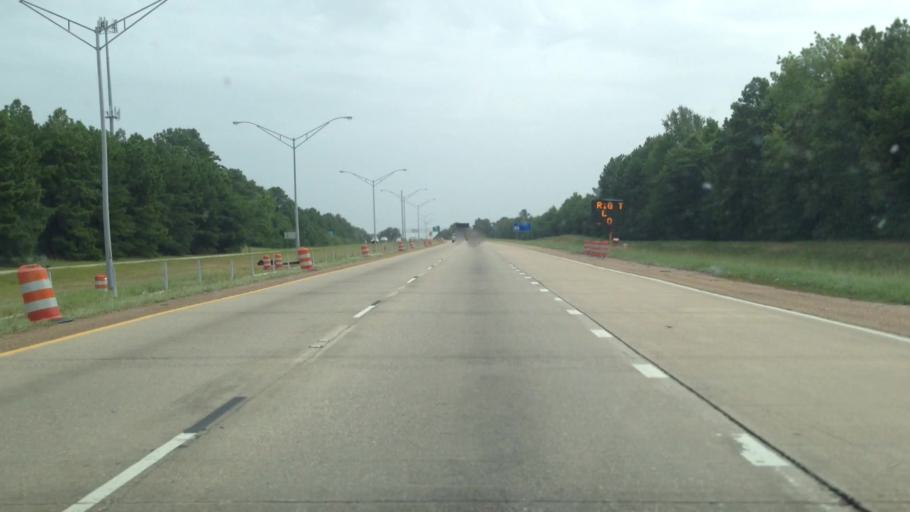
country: US
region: Louisiana
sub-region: Caddo Parish
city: Shreveport
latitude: 32.4894
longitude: -93.8253
